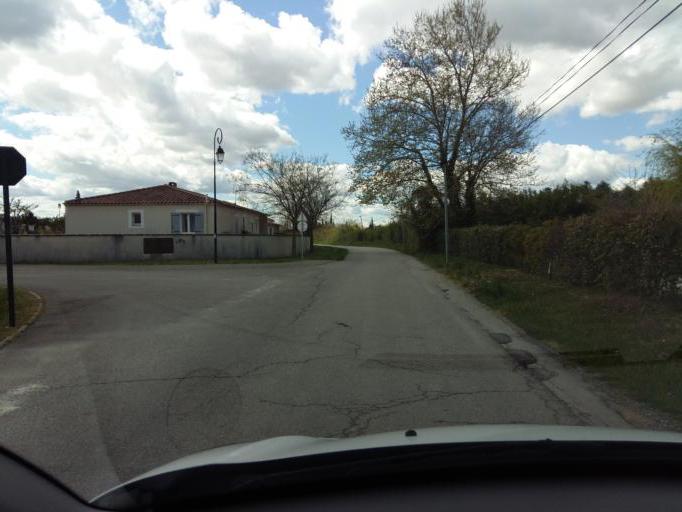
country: FR
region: Provence-Alpes-Cote d'Azur
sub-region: Departement du Vaucluse
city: Le Thor
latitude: 43.9280
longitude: 5.0115
